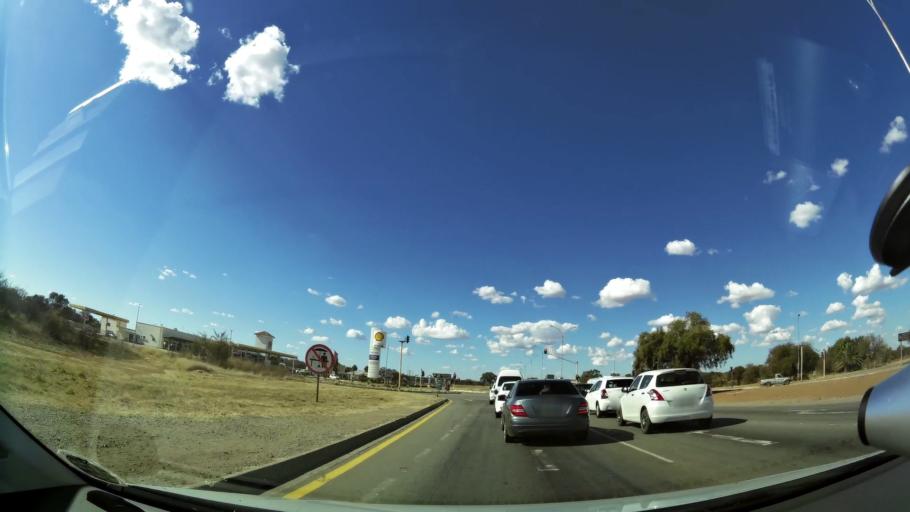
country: ZA
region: North-West
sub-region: Dr Kenneth Kaunda District Municipality
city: Klerksdorp
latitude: -26.8684
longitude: 26.6268
